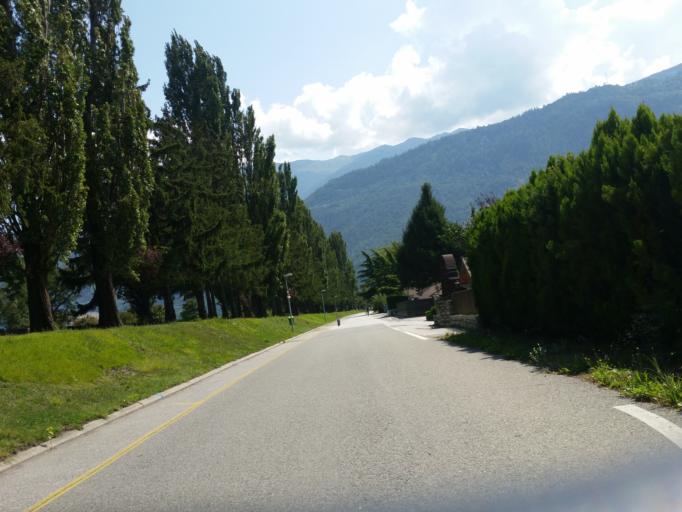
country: CH
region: Valais
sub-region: Conthey District
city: Ardon
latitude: 46.2129
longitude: 7.2647
